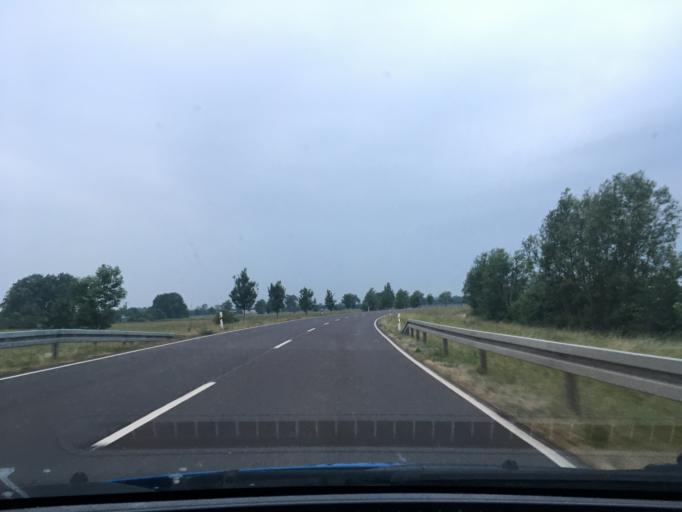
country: DE
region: Saxony-Anhalt
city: Salzwedel
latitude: 52.8683
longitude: 11.1685
